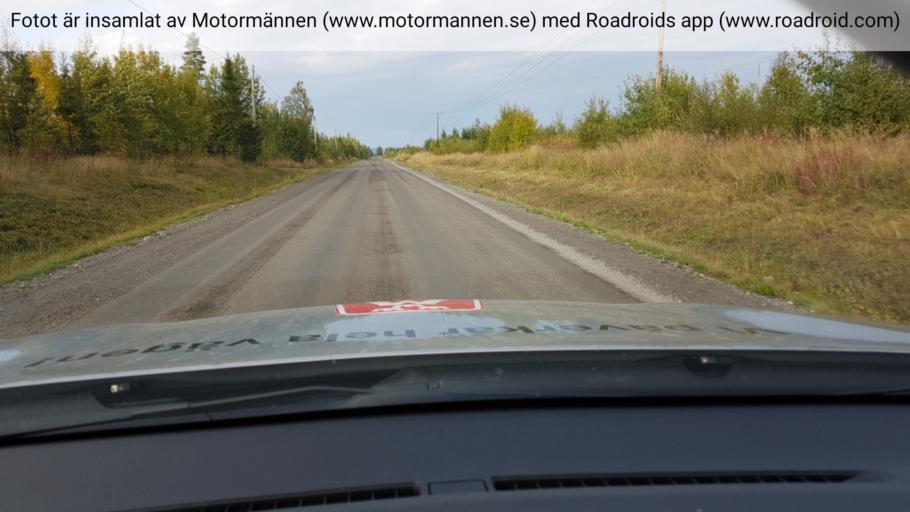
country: SE
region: Jaemtland
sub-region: Stroemsunds Kommun
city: Stroemsund
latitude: 63.9875
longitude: 15.8163
